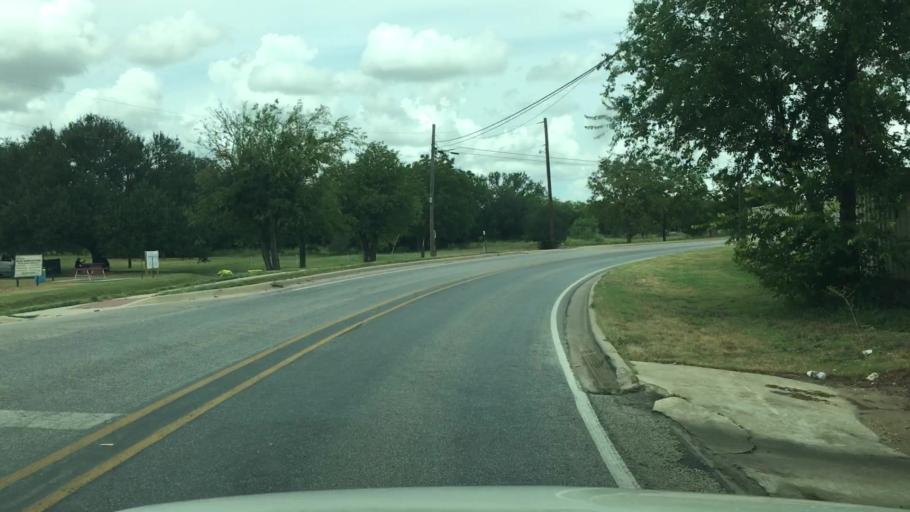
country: US
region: Texas
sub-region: McCulloch County
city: Brady
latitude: 31.1237
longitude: -99.3265
